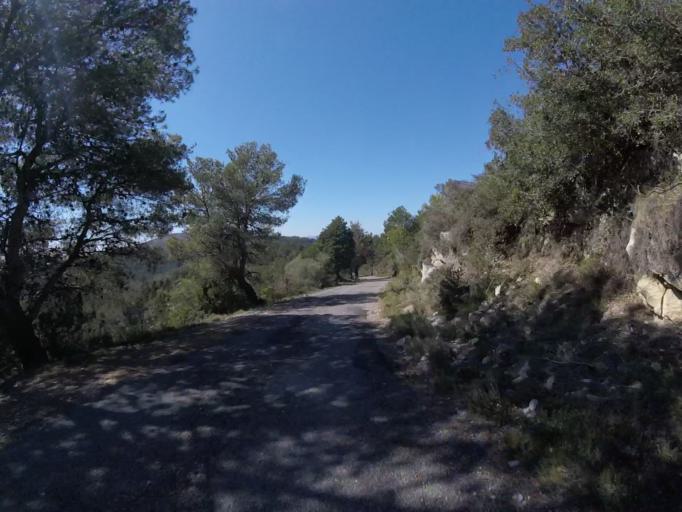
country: ES
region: Valencia
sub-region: Provincia de Castello
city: Cervera del Maestre
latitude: 40.4103
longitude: 0.2001
